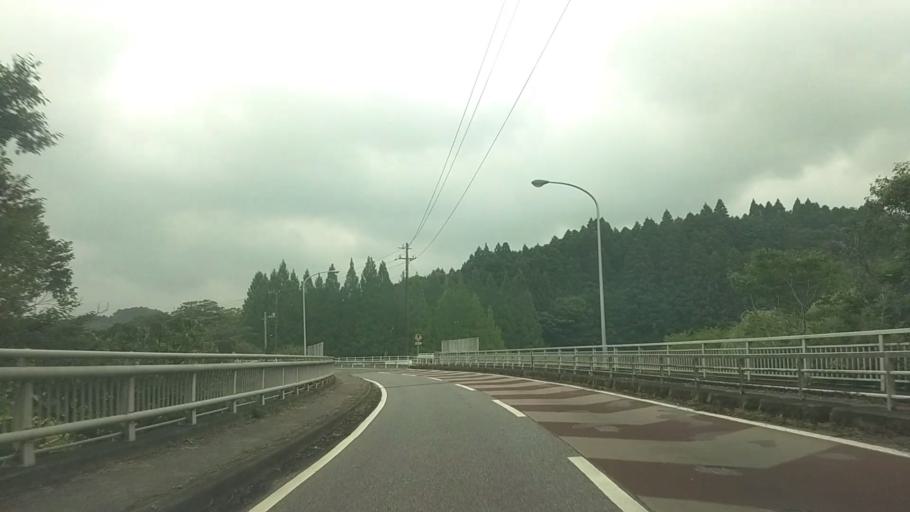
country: JP
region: Chiba
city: Kawaguchi
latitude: 35.2273
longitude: 140.0901
